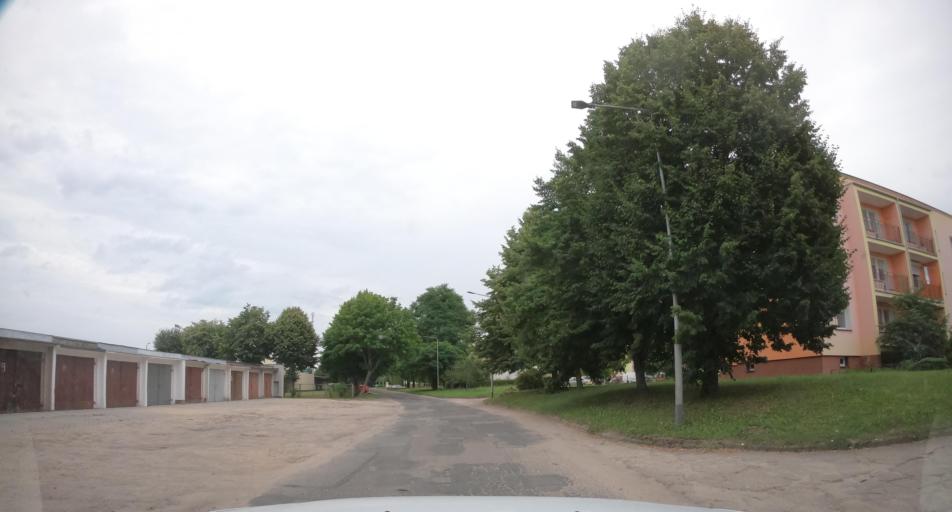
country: PL
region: West Pomeranian Voivodeship
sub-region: Powiat walecki
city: Walcz
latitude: 53.2750
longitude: 16.4508
